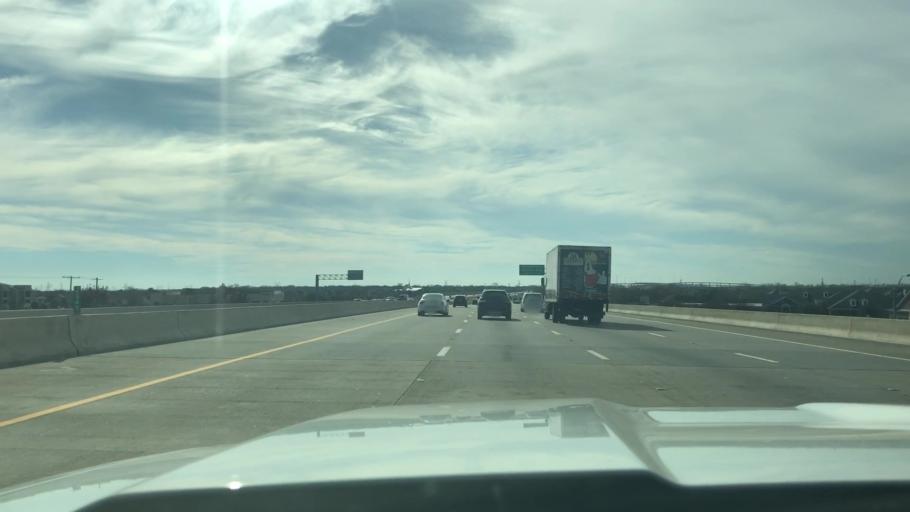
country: US
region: Texas
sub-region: Denton County
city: Lewisville
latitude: 33.0229
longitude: -96.9341
